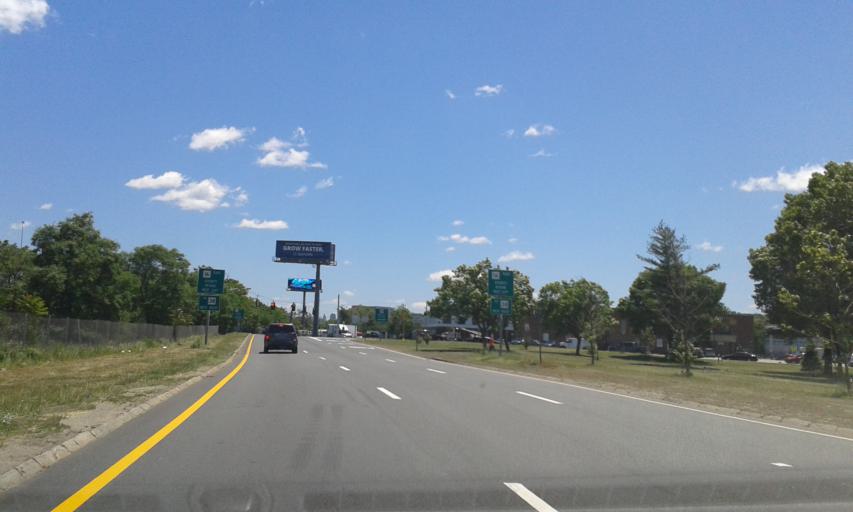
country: US
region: Massachusetts
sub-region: Middlesex County
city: Medford
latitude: 42.4076
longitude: -71.1020
